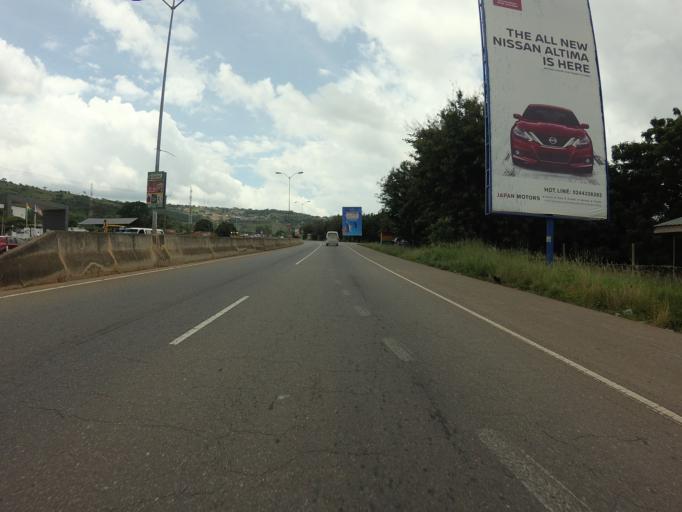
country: GH
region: Eastern
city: Aburi
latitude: 5.7817
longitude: -0.1816
